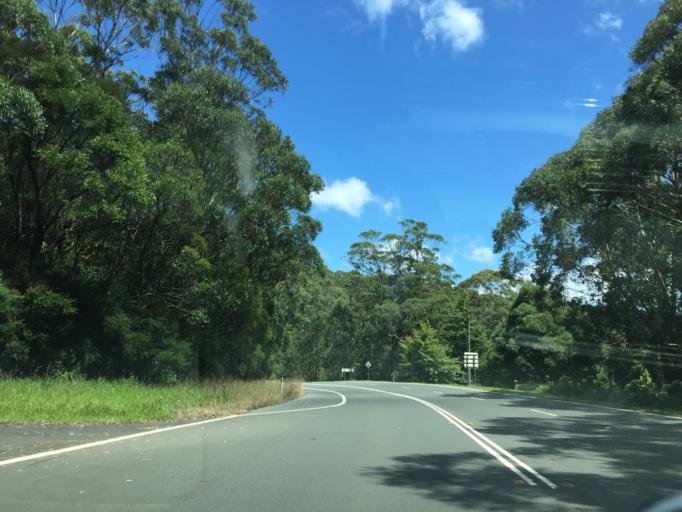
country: AU
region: New South Wales
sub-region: Blue Mountains Municipality
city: Blackheath
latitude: -33.5470
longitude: 150.4238
